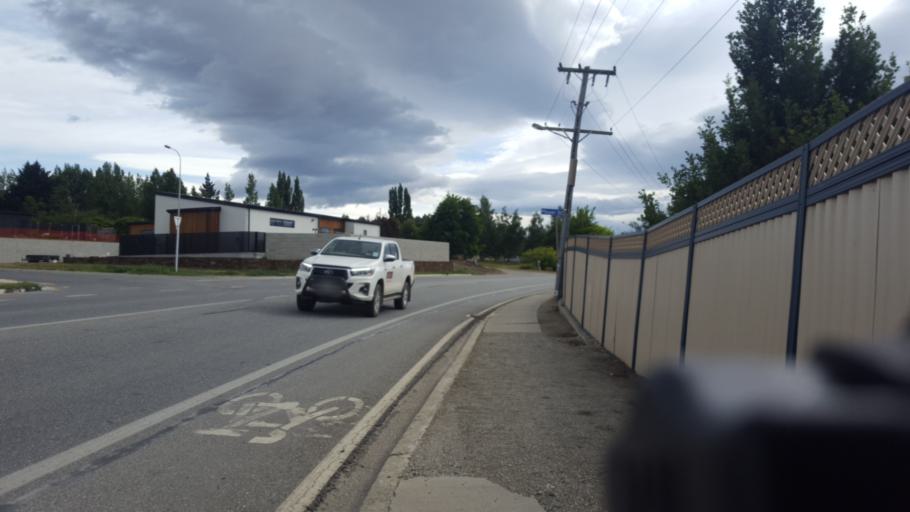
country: NZ
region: Otago
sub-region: Queenstown-Lakes District
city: Wanaka
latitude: -45.2458
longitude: 169.4025
